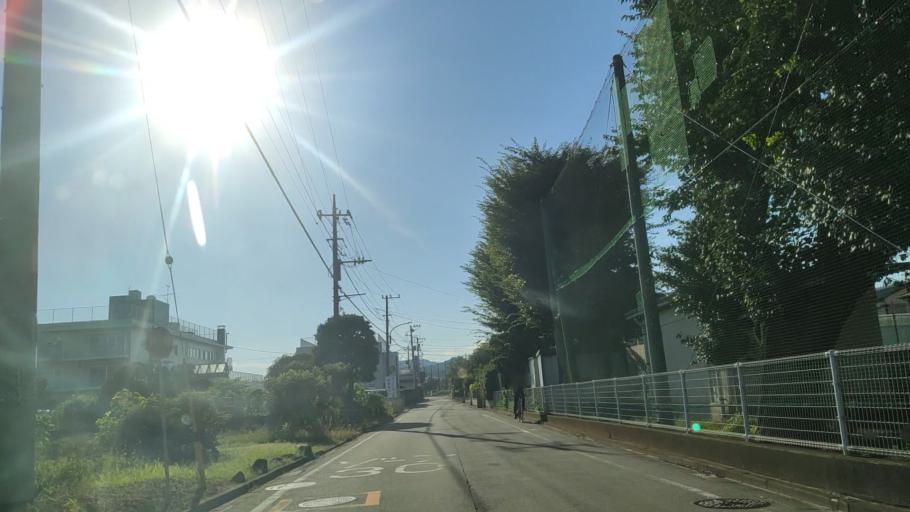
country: JP
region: Tokyo
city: Hachioji
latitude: 35.5915
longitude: 139.3166
